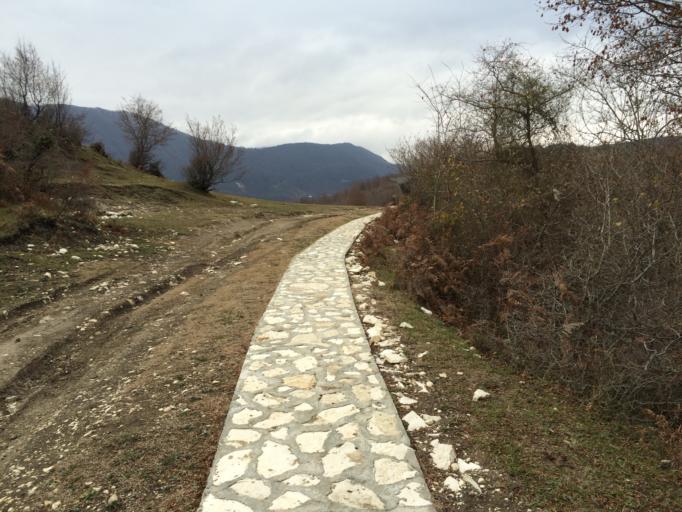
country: GE
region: Imereti
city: Tsqaltubo
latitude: 42.4535
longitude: 42.5494
